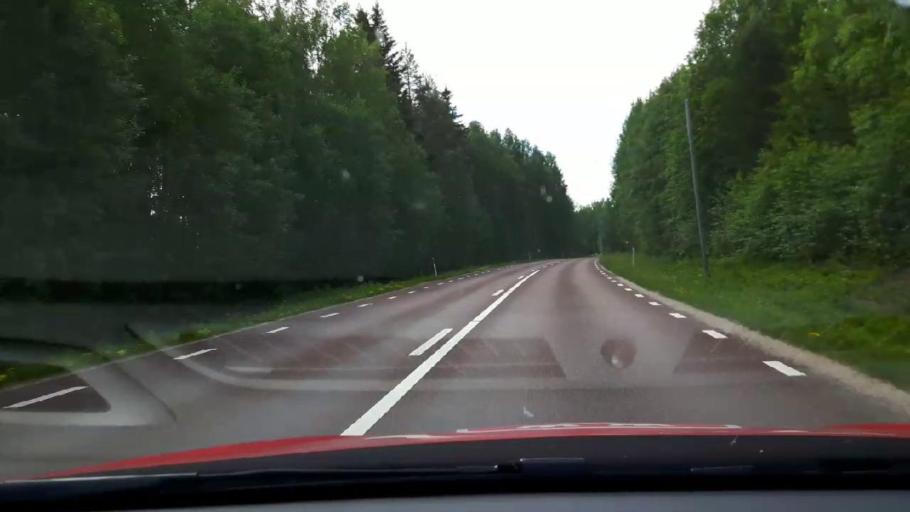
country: SE
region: Jaemtland
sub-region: Harjedalens Kommun
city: Sveg
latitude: 62.0718
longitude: 14.9392
